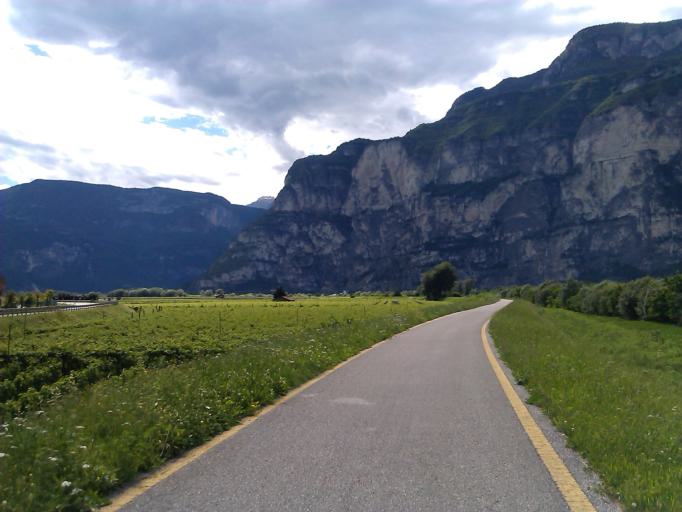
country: IT
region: Trentino-Alto Adige
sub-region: Provincia di Trento
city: Rovere della Luna
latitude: 46.2260
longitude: 11.1639
